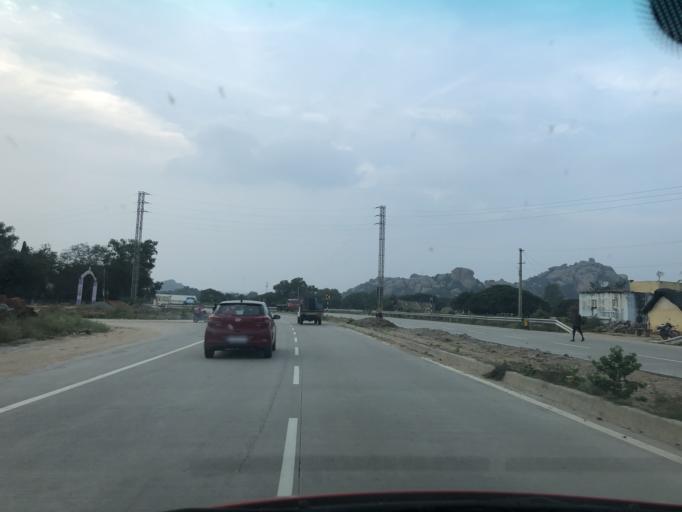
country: IN
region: Andhra Pradesh
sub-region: Chittoor
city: Chittoor
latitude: 13.1975
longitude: 78.9993
